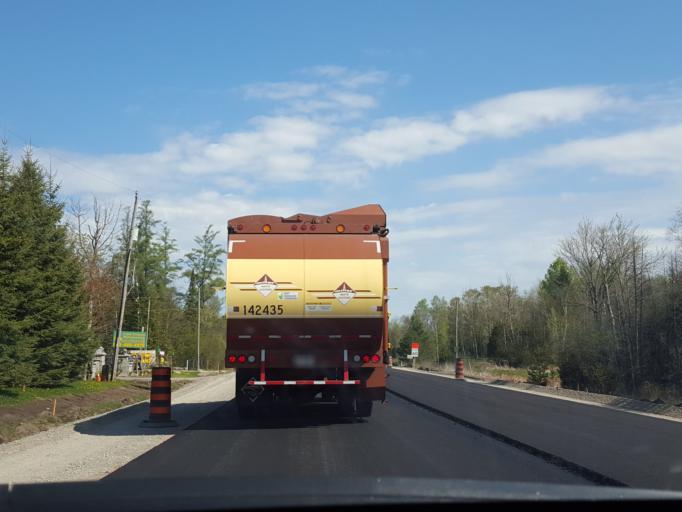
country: CA
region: Ontario
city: Uxbridge
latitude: 44.0699
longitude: -78.9345
